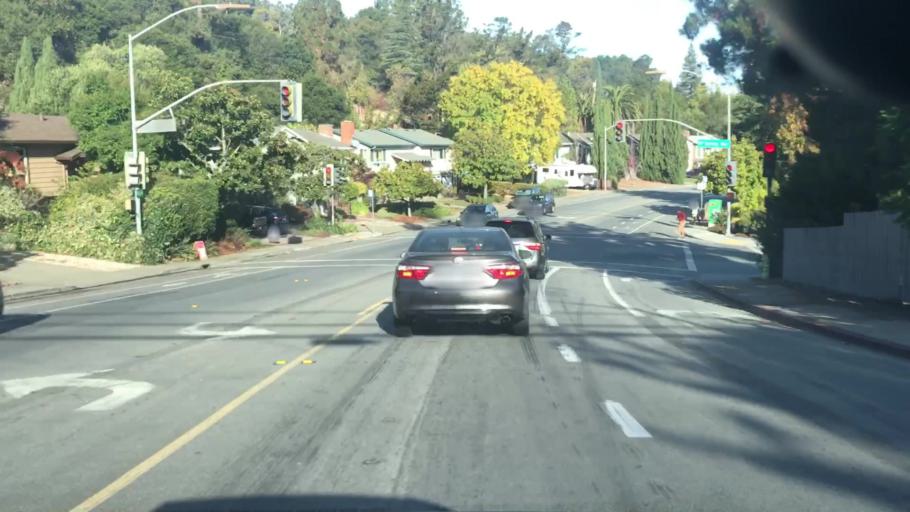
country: US
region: California
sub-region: San Mateo County
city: Emerald Lake Hills
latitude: 37.4607
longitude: -122.2497
